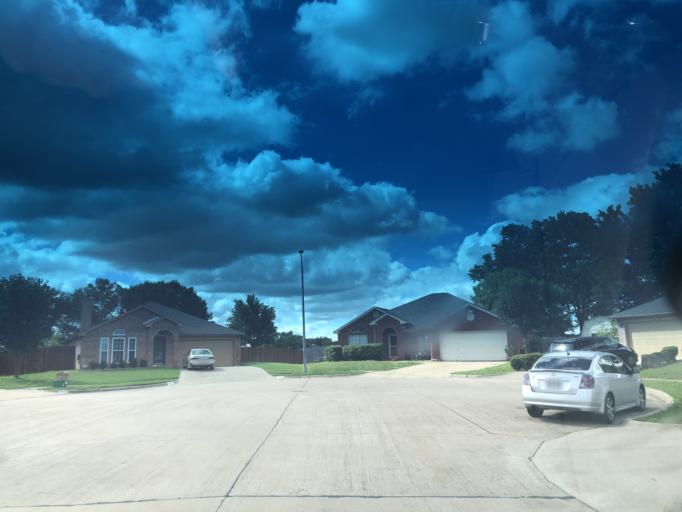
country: US
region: Texas
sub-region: Dallas County
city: Grand Prairie
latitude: 32.6959
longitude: -97.0335
